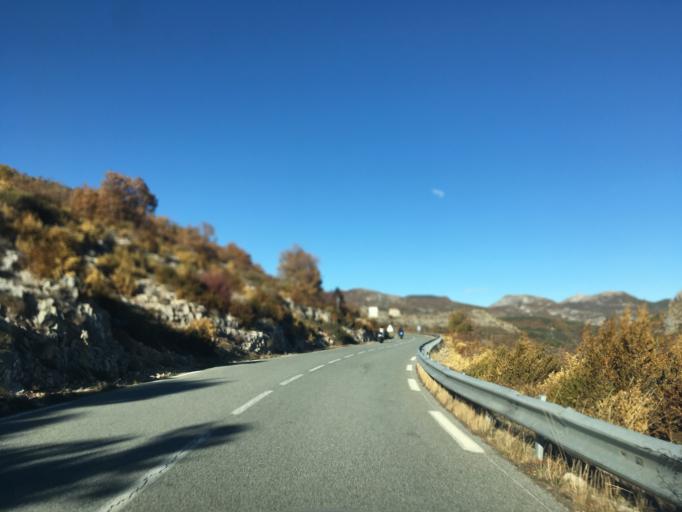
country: FR
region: Provence-Alpes-Cote d'Azur
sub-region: Departement du Var
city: Bargemon
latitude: 43.7025
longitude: 6.5085
